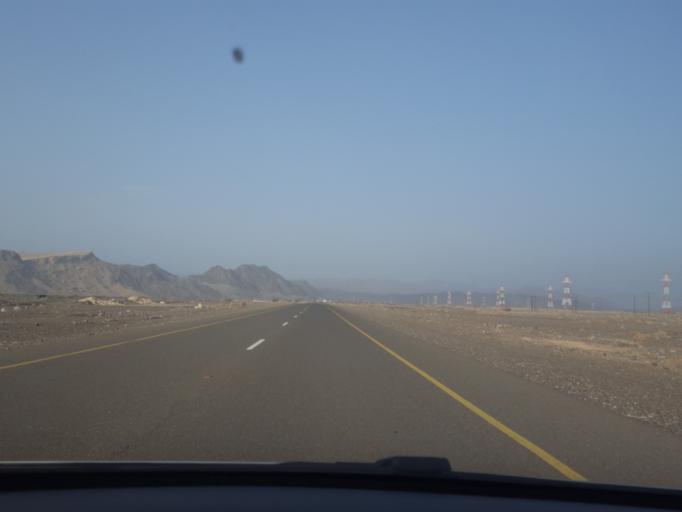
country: AE
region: Abu Dhabi
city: Al Ain
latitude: 24.0435
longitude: 56.0324
